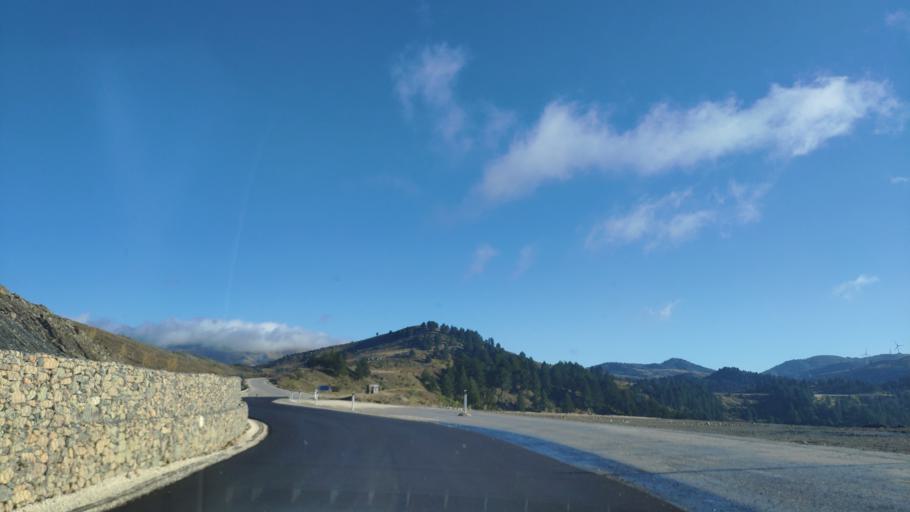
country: GR
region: Epirus
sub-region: Nomos Ioanninon
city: Metsovo
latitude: 39.7908
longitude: 21.1646
